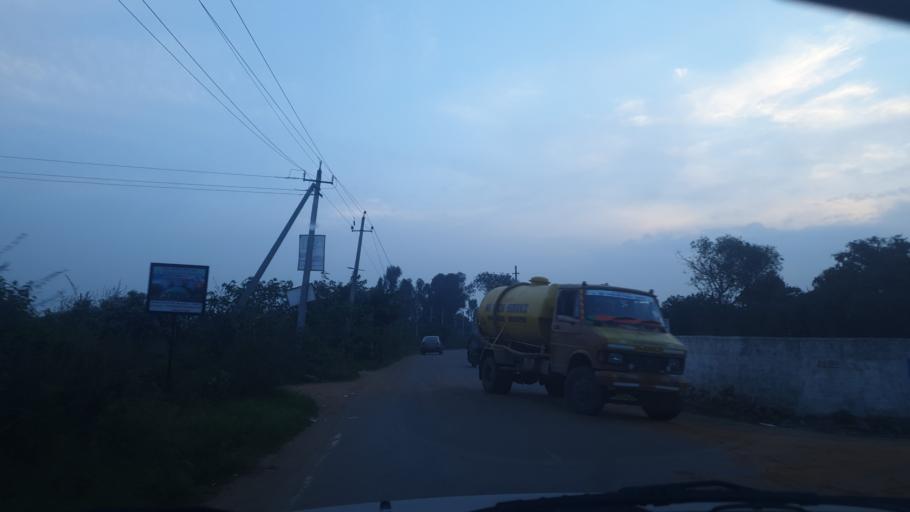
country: IN
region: Karnataka
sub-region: Bangalore Urban
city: Yelahanka
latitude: 13.0619
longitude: 77.6867
